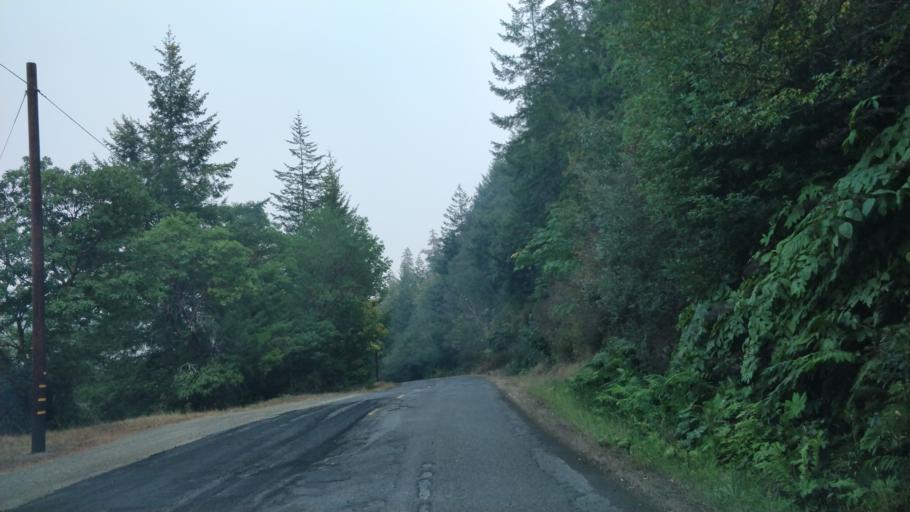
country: US
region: California
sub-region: Humboldt County
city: Rio Dell
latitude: 40.3109
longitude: -124.2757
